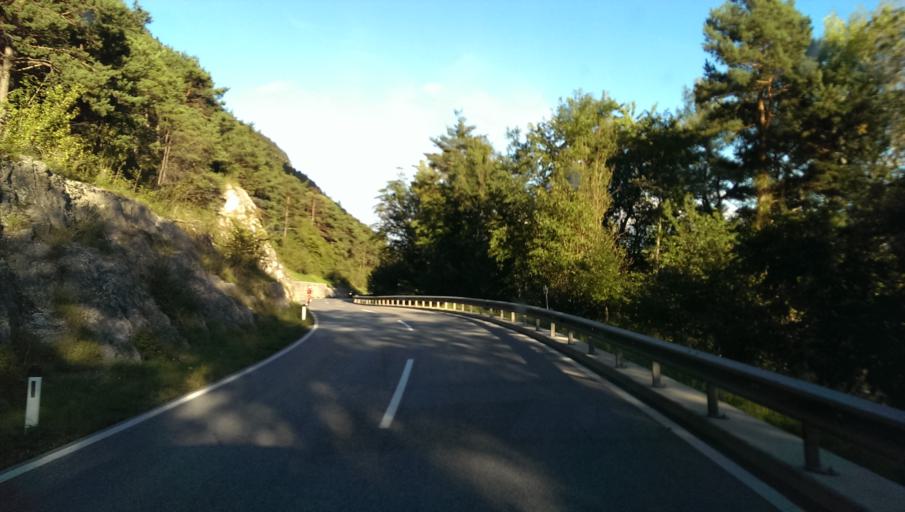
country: AT
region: Tyrol
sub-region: Politischer Bezirk Innsbruck Land
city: Kematen in Tirol
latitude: 47.2669
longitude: 11.2777
